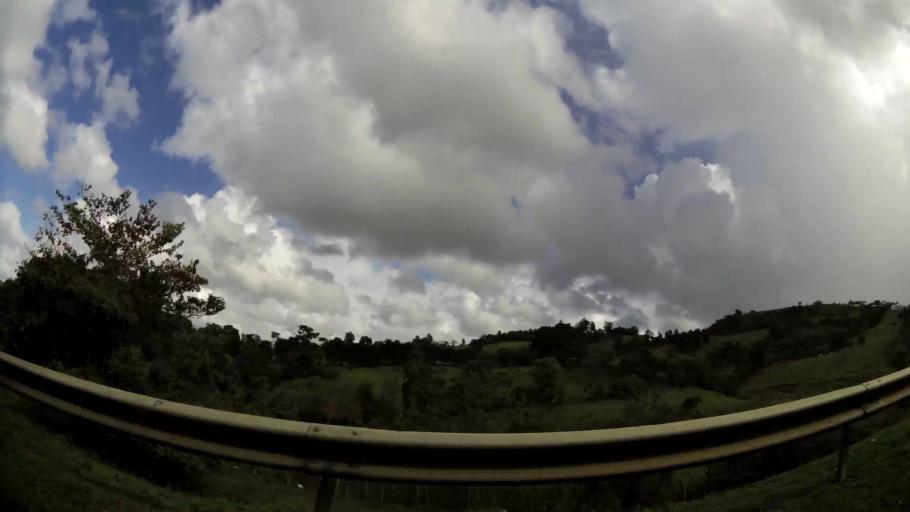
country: MQ
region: Martinique
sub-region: Martinique
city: Sainte-Luce
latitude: 14.5030
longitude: -60.9802
